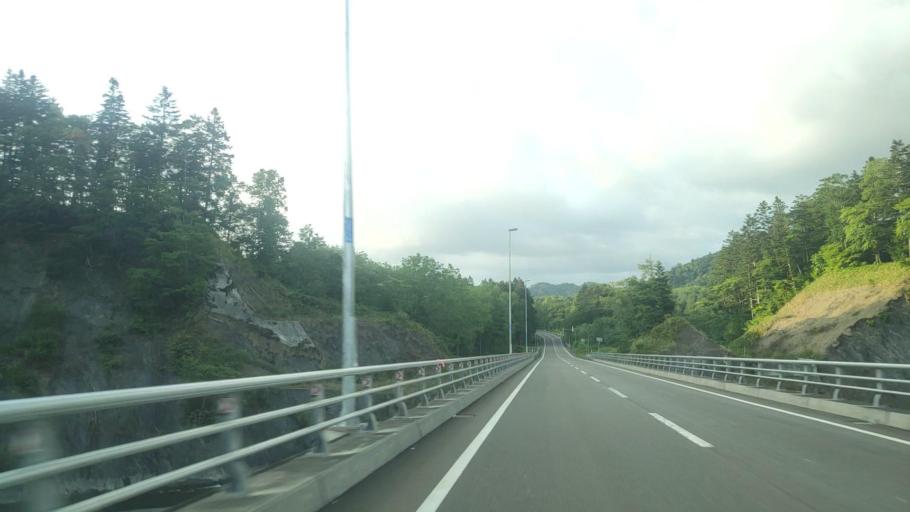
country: JP
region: Hokkaido
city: Bibai
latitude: 43.1096
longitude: 142.0987
